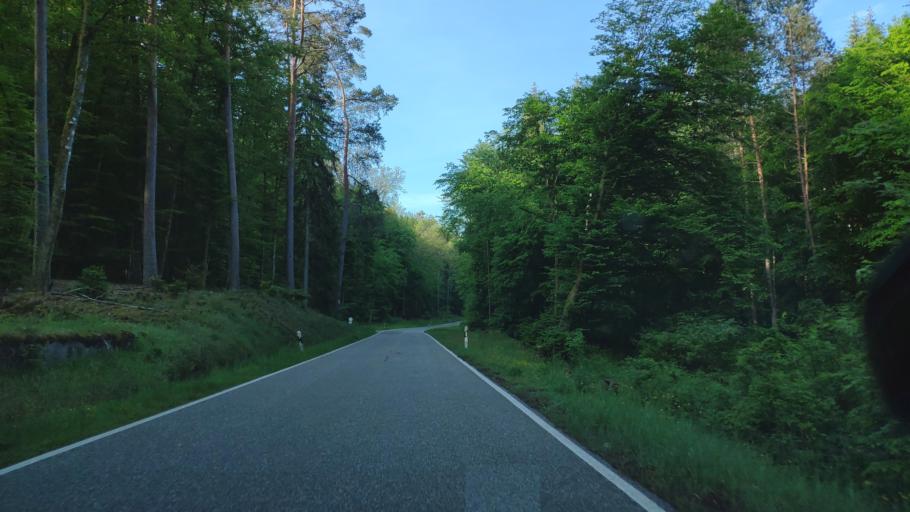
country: DE
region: Rheinland-Pfalz
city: Ruppertsweiler
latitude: 49.1574
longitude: 7.7129
